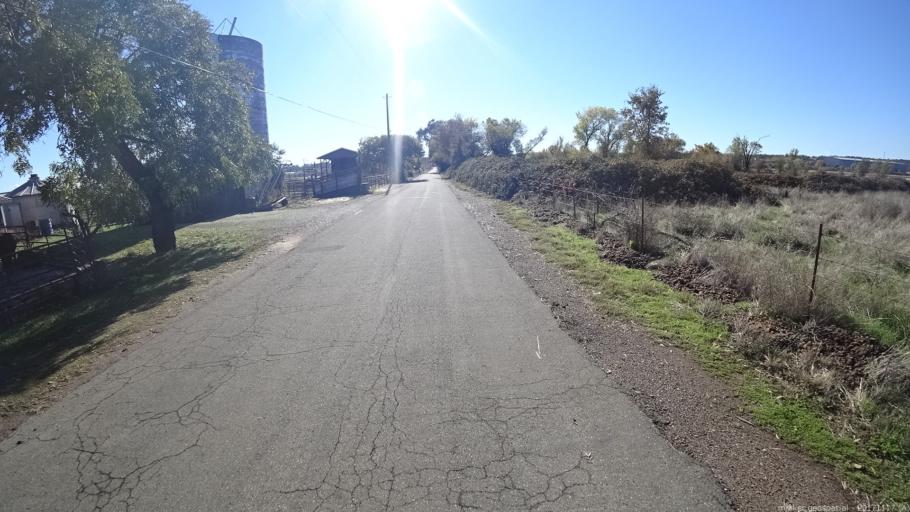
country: US
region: California
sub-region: Shasta County
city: Anderson
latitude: 40.4292
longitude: -122.2593
